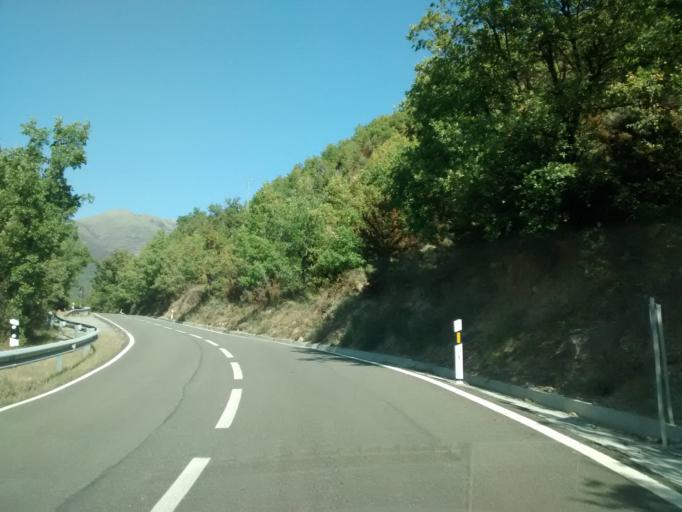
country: ES
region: Aragon
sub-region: Provincia de Huesca
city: Fiscal
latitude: 42.5182
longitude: -0.1283
